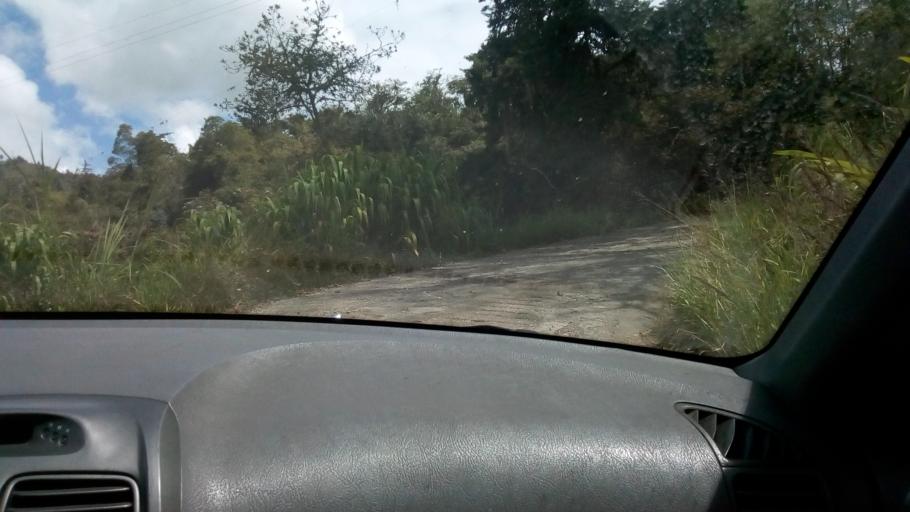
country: CO
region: Cundinamarca
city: Tenza
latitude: 5.0941
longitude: -73.4244
